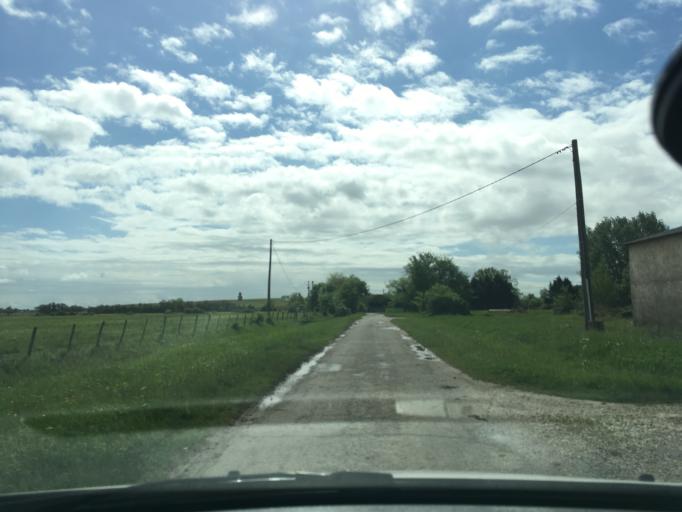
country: FR
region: Aquitaine
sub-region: Departement de la Gironde
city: Saint-Estephe
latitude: 45.3247
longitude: -0.8007
